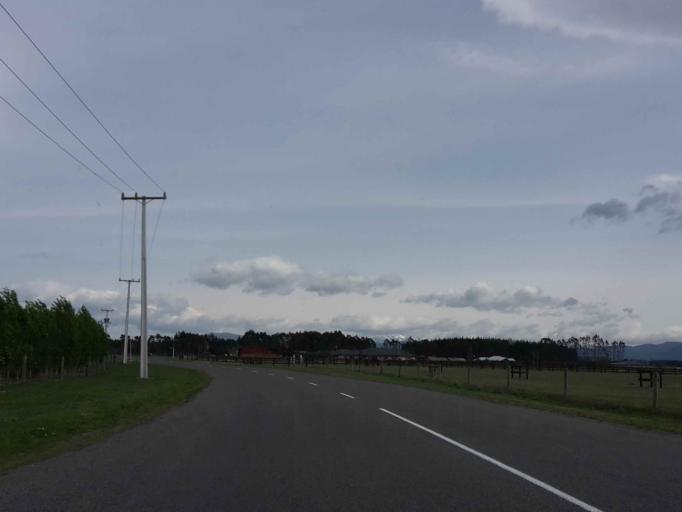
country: NZ
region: Canterbury
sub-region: Waimakariri District
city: Kaiapoi
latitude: -43.3504
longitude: 172.5105
